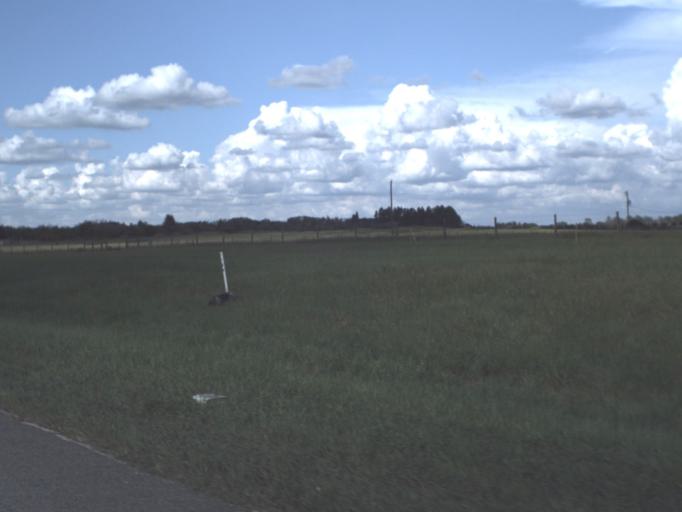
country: US
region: Florida
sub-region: Polk County
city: Polk City
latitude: 28.2743
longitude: -81.8287
